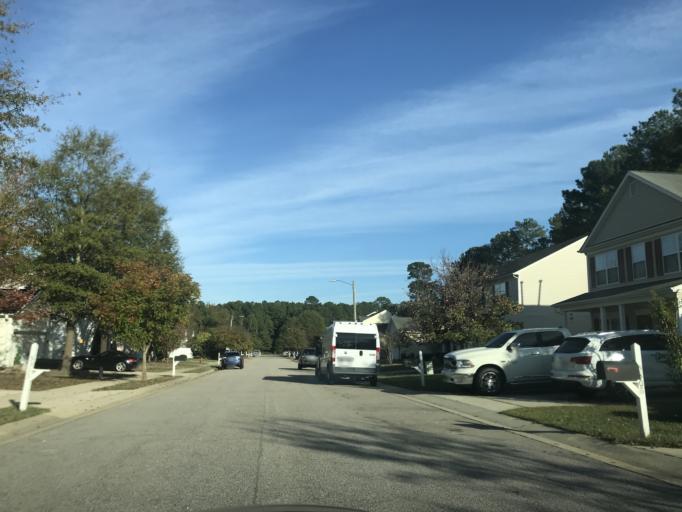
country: US
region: North Carolina
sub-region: Wake County
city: Wake Forest
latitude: 35.8968
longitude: -78.5484
